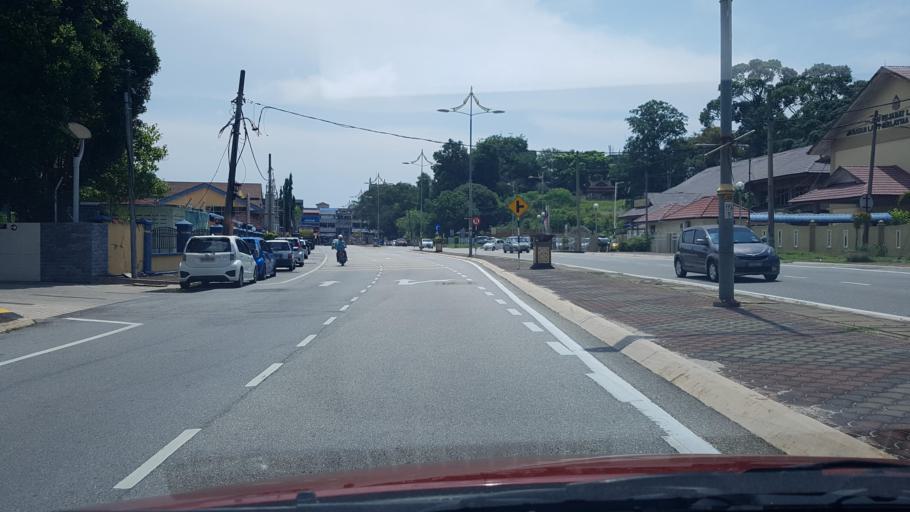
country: MY
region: Terengganu
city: Kuala Terengganu
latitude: 5.3286
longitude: 103.1327
